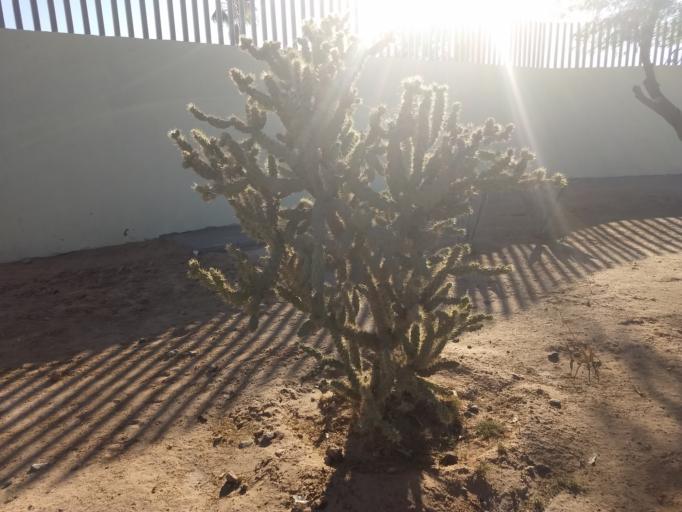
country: MX
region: Baja California
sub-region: Mexicali
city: Islas Agrarias Grupo A
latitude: 32.6281
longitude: -115.2474
